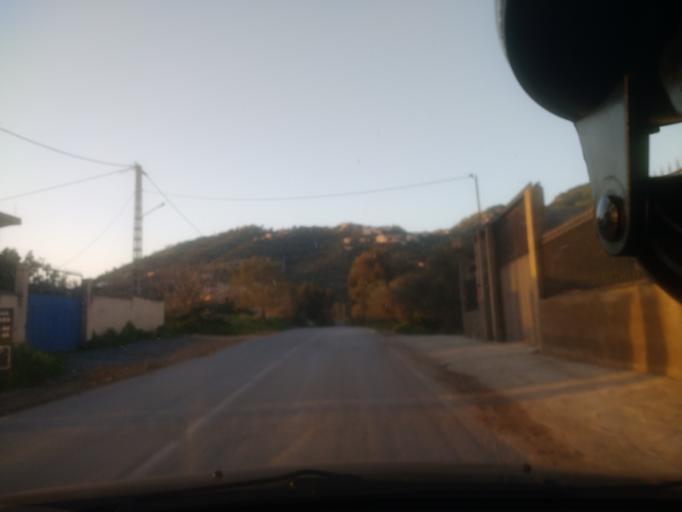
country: DZ
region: Boumerdes
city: Makouda
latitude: 36.7754
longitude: 4.0647
